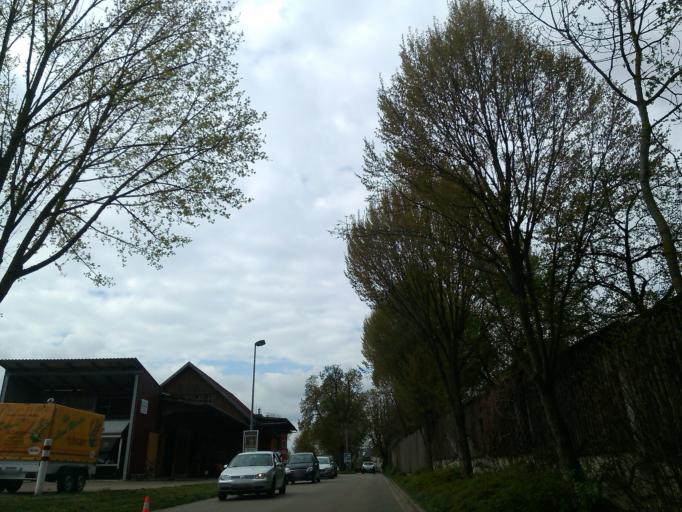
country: DE
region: Baden-Wuerttemberg
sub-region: Tuebingen Region
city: Langenau
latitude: 48.4945
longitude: 10.1273
